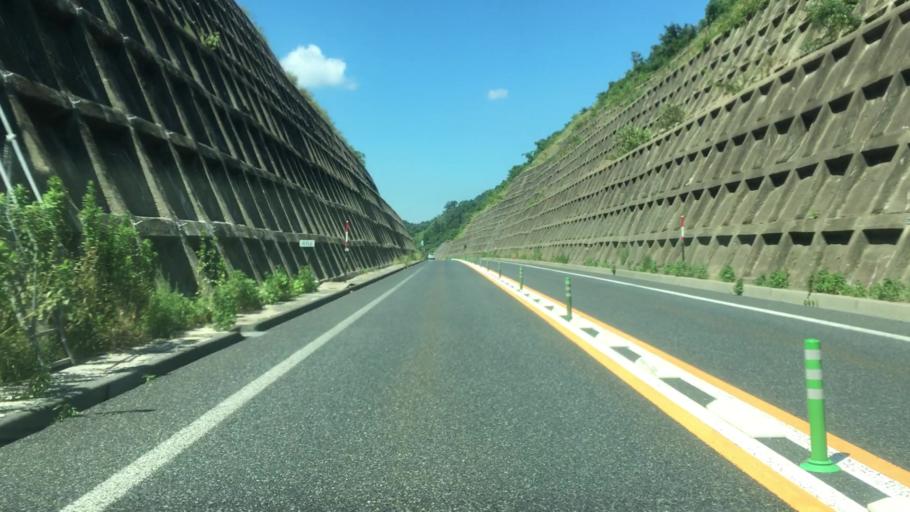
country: JP
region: Tottori
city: Tottori
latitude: 35.3585
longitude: 134.1988
